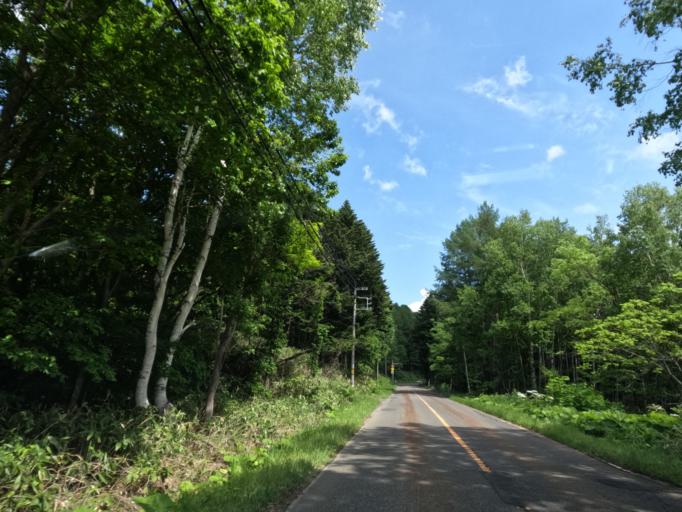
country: JP
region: Hokkaido
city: Takikawa
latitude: 43.5785
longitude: 141.8318
